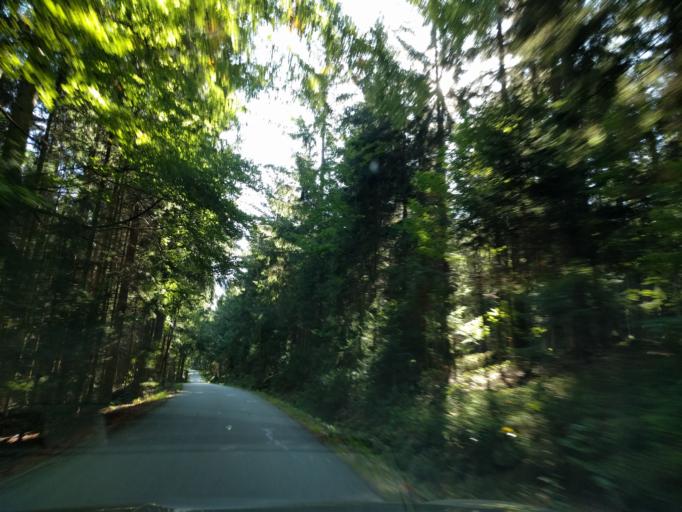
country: DE
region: Bavaria
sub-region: Upper Palatinate
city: Hohenwarth
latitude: 49.1841
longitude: 12.9304
